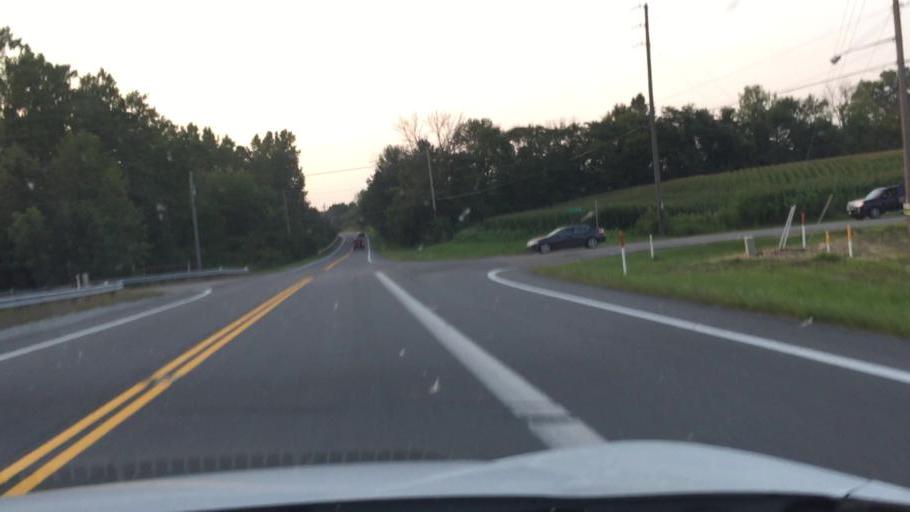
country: US
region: Ohio
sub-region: Madison County
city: Choctaw Lake
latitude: 39.9475
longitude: -83.5030
